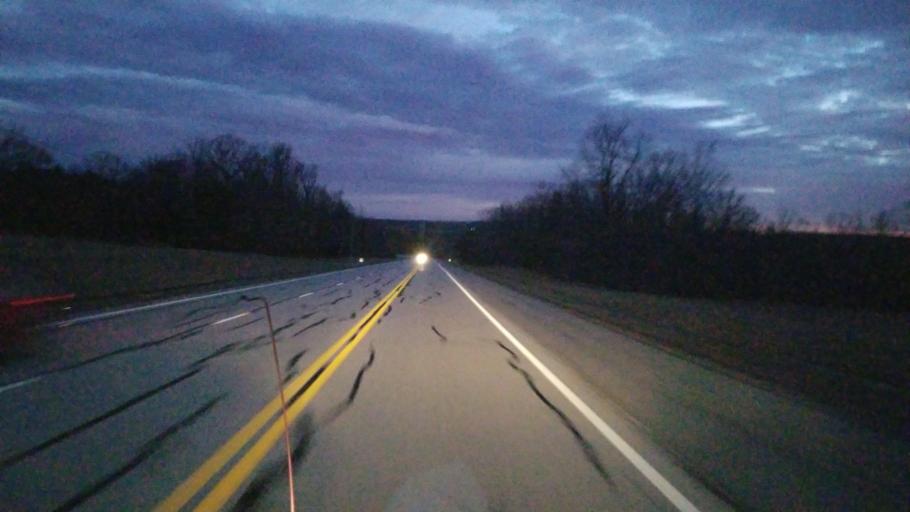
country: US
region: Tennessee
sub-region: Sequatchie County
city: Dunlap
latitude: 35.5144
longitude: -85.4722
